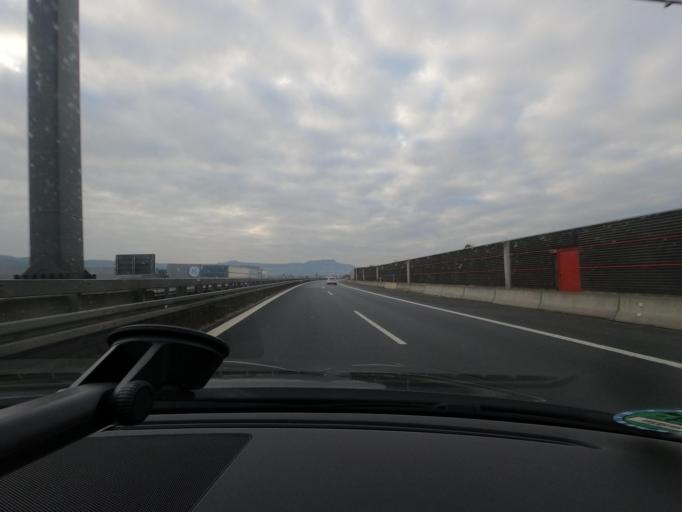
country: DE
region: Bavaria
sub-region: Upper Franconia
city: Lichtenfels
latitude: 50.1317
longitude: 11.0351
